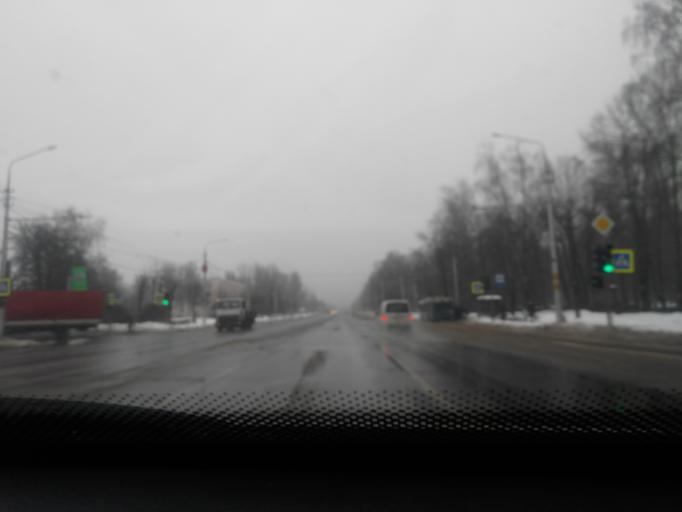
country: BY
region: Mogilev
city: Babruysk
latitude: 53.1750
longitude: 29.2008
